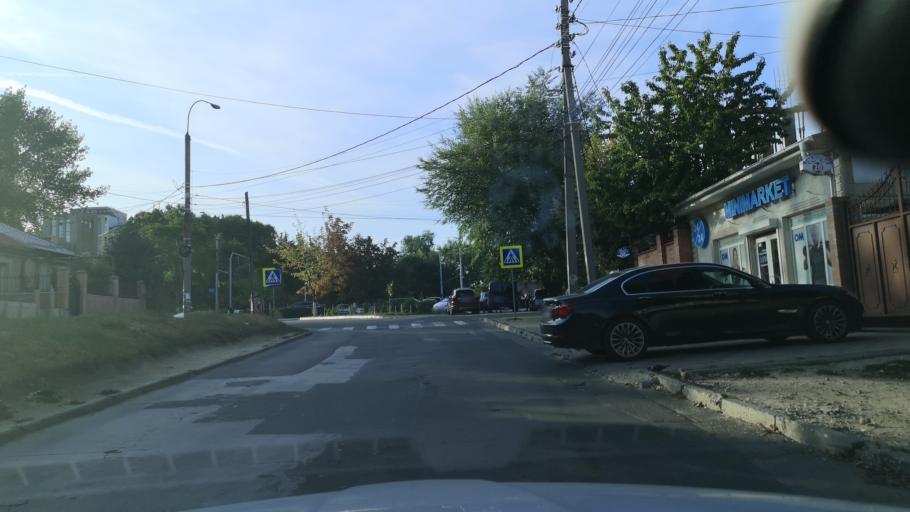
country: MD
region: Chisinau
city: Chisinau
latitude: 47.0117
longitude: 28.8466
